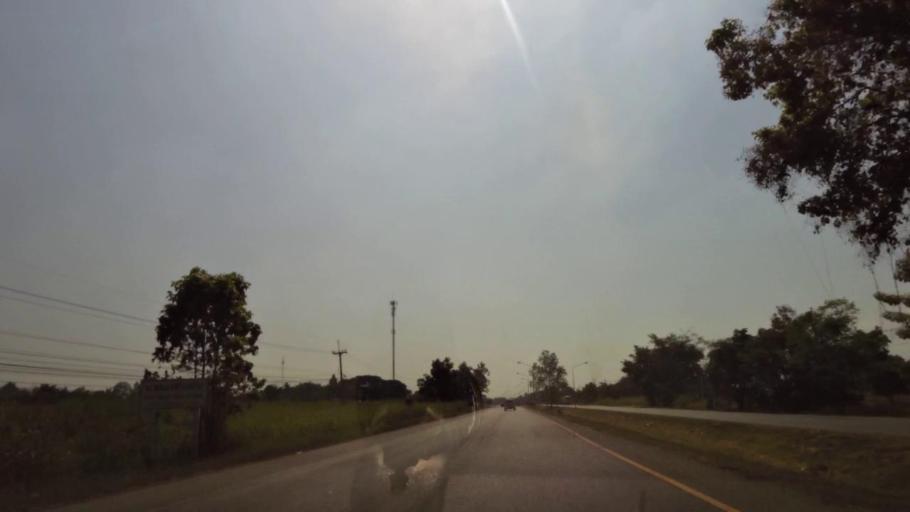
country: TH
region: Phichit
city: Wachira Barami
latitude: 16.3601
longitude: 100.1299
